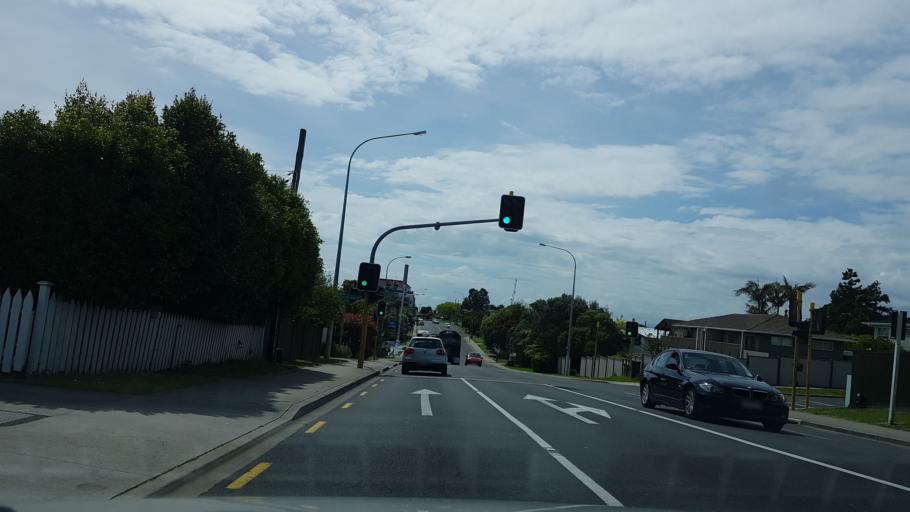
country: NZ
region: Auckland
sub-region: Auckland
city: North Shore
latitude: -36.8109
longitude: 174.7167
